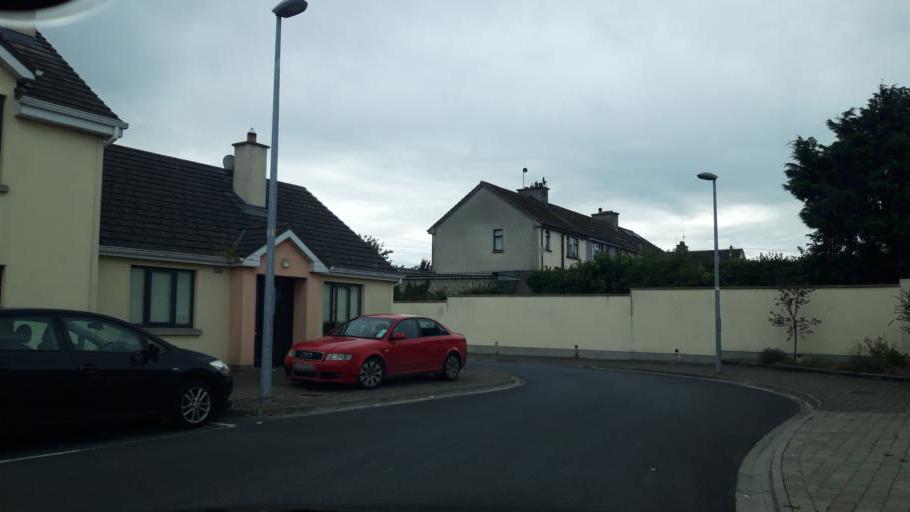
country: IE
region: Leinster
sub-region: Kilkenny
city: Ballyragget
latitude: 52.7915
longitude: -7.3298
